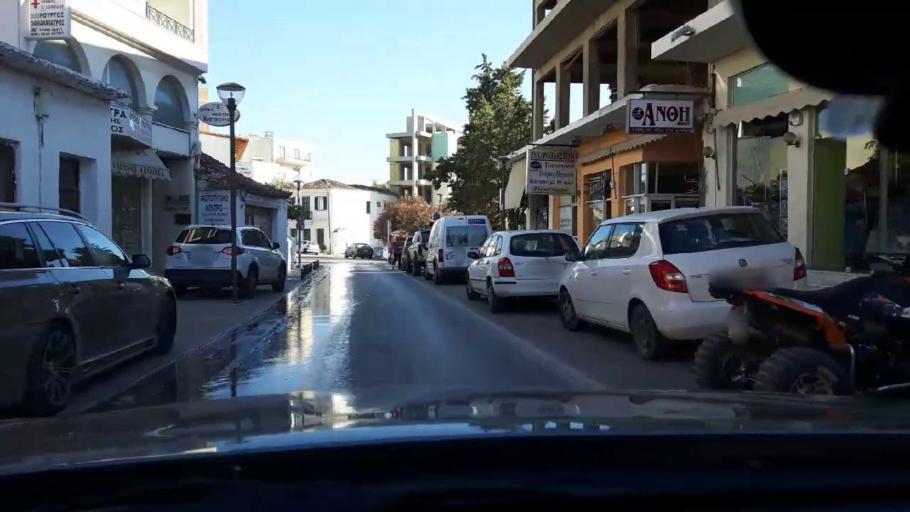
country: GR
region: Attica
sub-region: Nomarchia Anatolikis Attikis
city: Markopoulo
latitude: 37.8817
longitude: 23.9327
